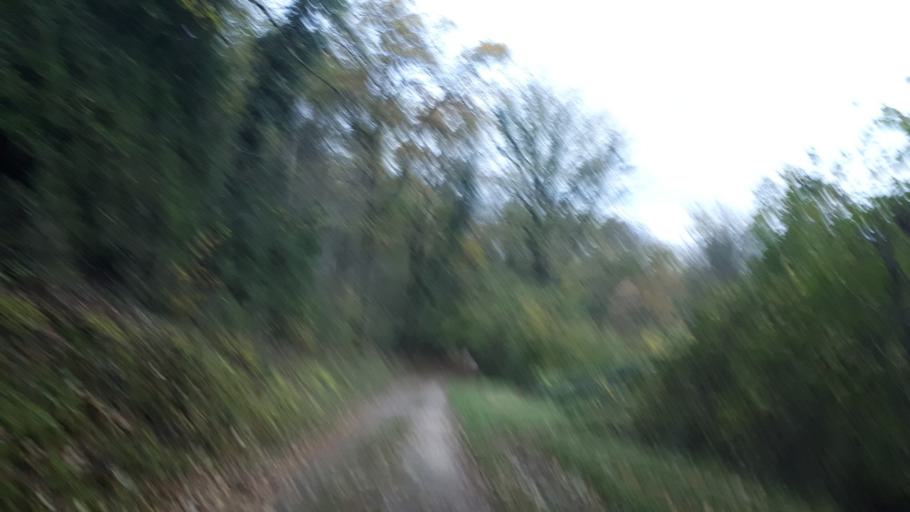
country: FR
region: Centre
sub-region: Departement du Loir-et-Cher
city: Lunay
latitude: 47.7655
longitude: 0.9364
